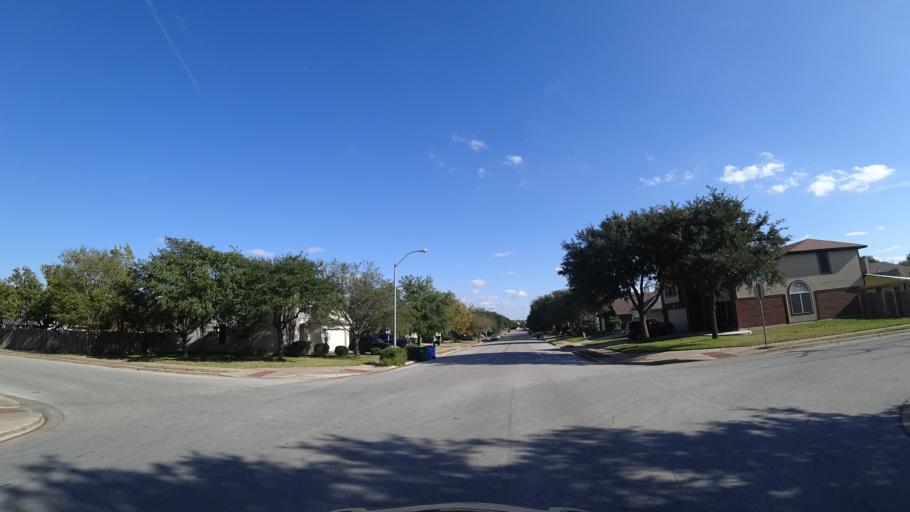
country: US
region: Texas
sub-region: Travis County
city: Wells Branch
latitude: 30.4607
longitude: -97.6850
